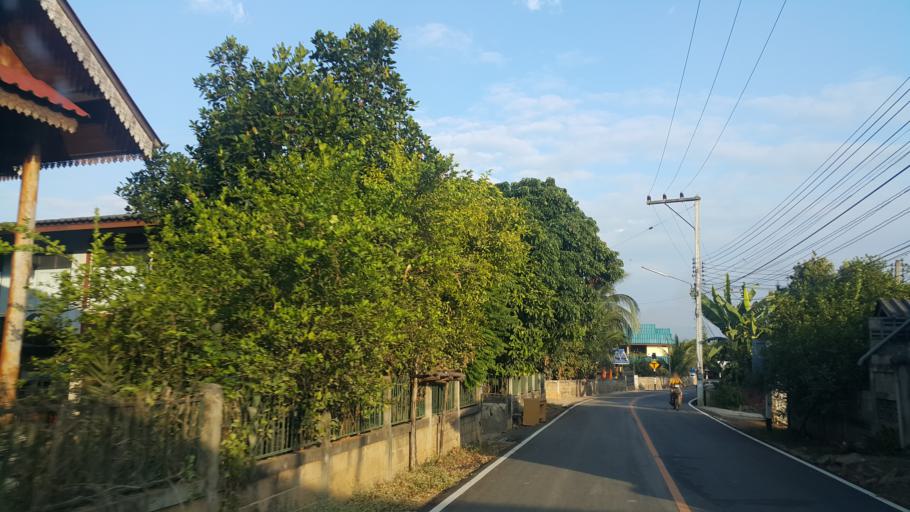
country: TH
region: Lampang
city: Sop Prap
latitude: 17.9433
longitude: 99.3421
